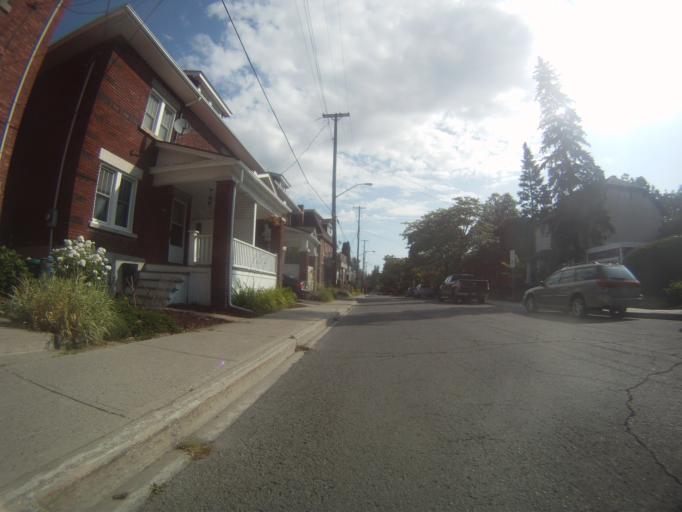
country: CA
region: Ontario
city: Ottawa
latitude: 45.3980
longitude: -75.6912
